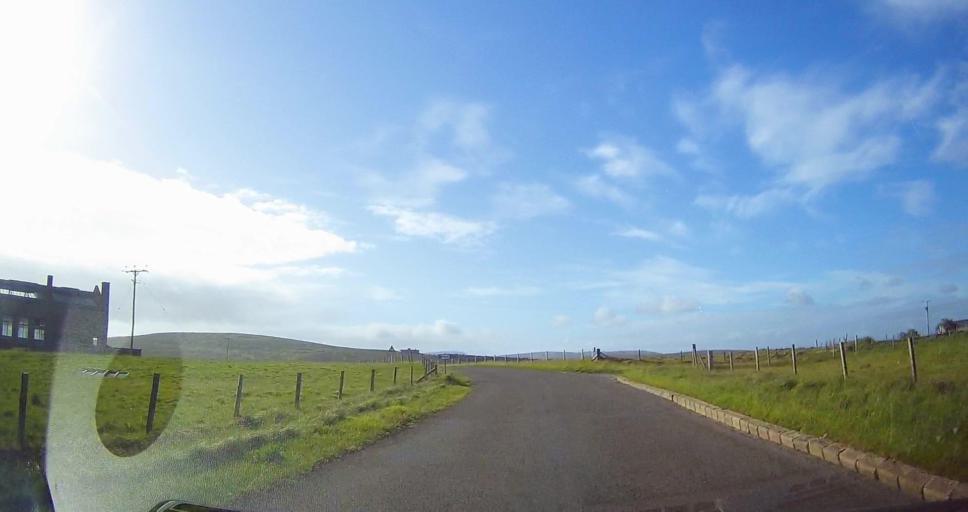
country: GB
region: Scotland
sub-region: Orkney Islands
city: Stromness
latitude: 58.8223
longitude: -3.2062
